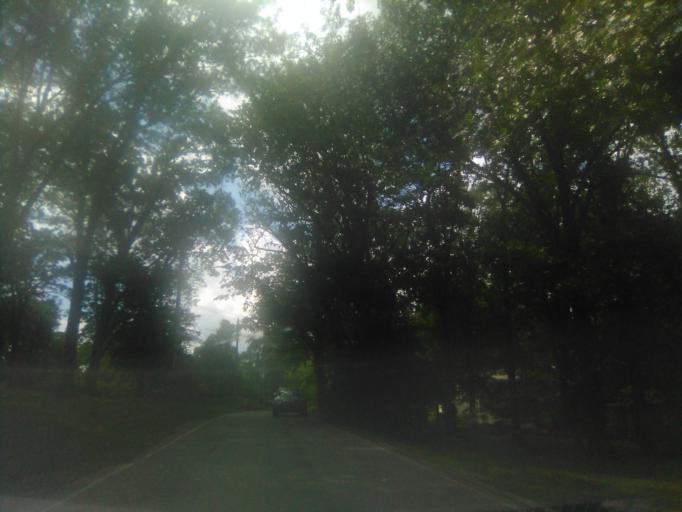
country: US
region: Tennessee
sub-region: Davidson County
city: Belle Meade
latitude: 36.1023
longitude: -86.8476
